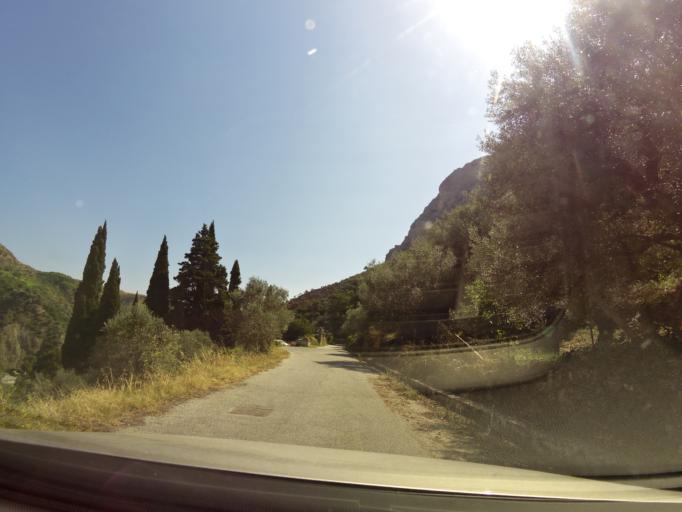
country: IT
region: Calabria
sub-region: Provincia di Reggio Calabria
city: Bivongi
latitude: 38.4848
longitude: 16.4582
